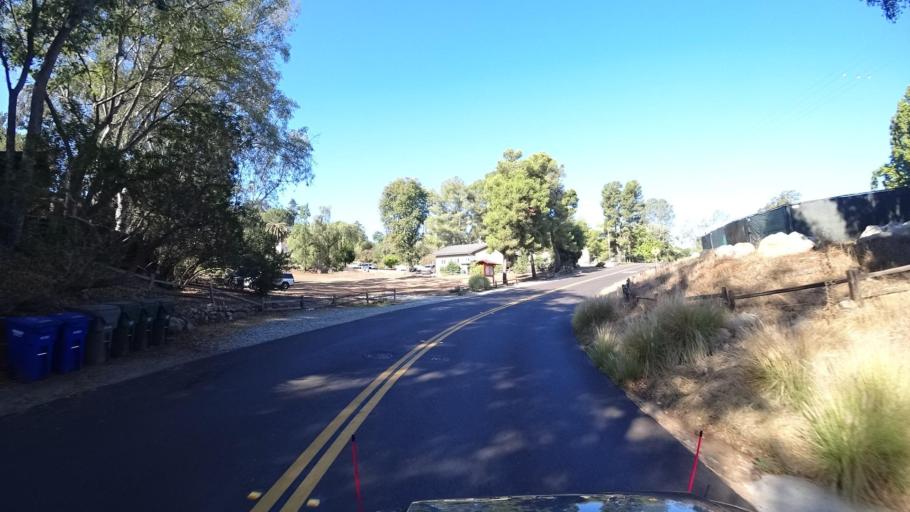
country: US
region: California
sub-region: San Diego County
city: Casa de Oro-Mount Helix
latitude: 32.7698
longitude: -116.9792
